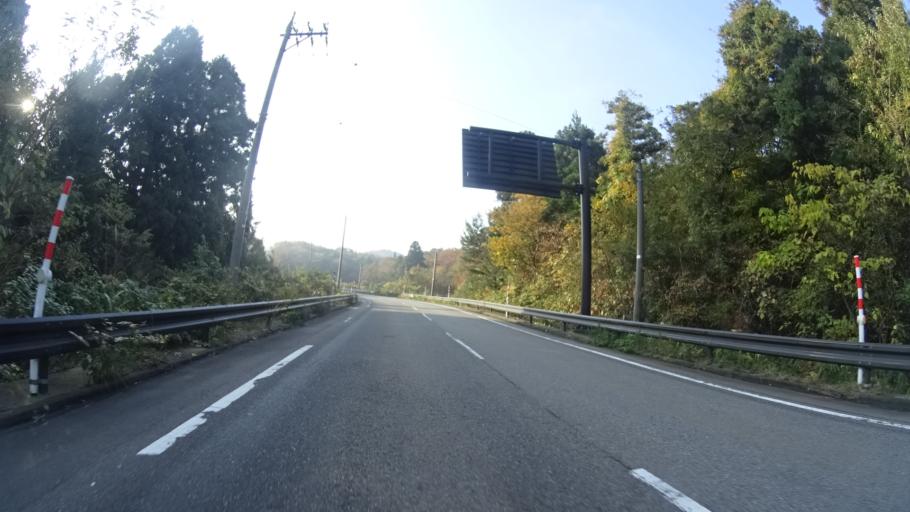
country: JP
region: Ishikawa
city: Nanao
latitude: 37.0249
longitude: 136.9851
